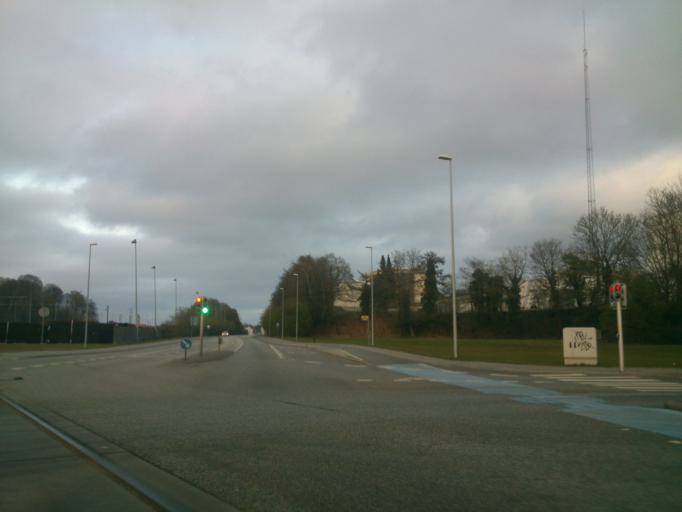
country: DK
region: South Denmark
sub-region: Fredericia Kommune
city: Fredericia
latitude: 55.5618
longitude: 9.7406
